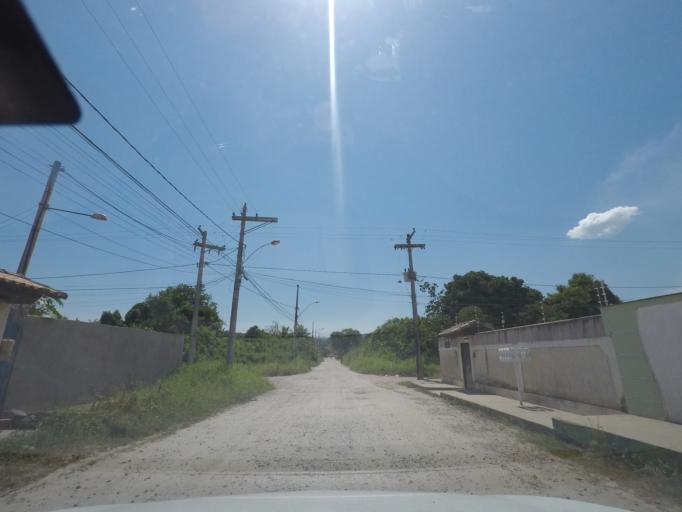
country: BR
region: Rio de Janeiro
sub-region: Marica
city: Marica
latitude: -22.9519
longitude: -42.9593
